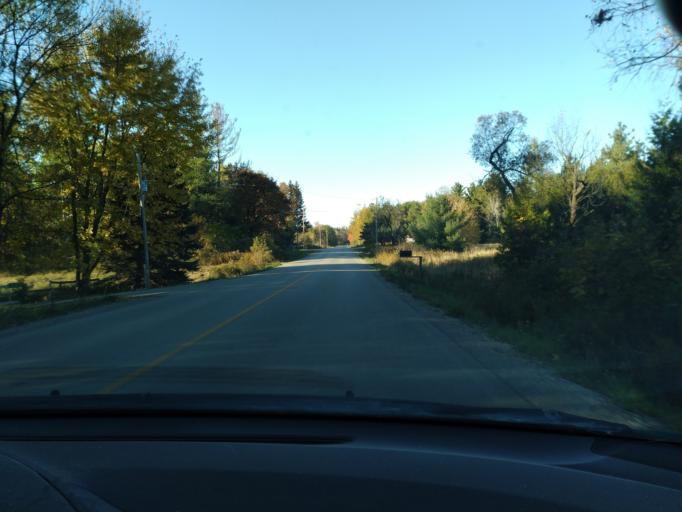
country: CA
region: Ontario
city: Bradford West Gwillimbury
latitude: 44.0493
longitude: -79.7349
